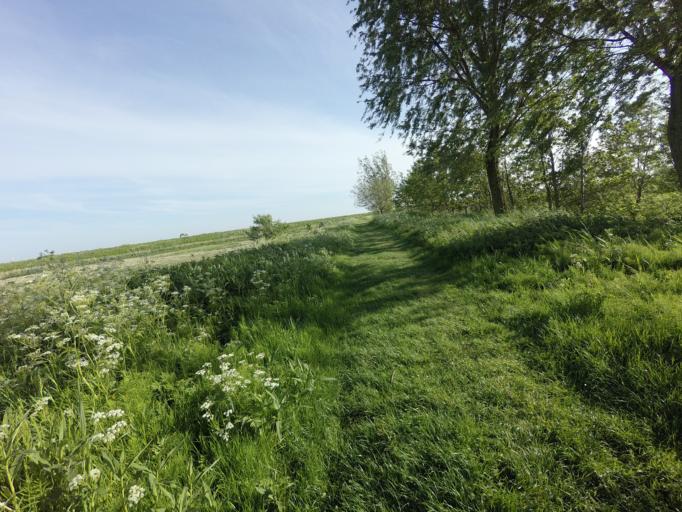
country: NL
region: North Brabant
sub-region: Gemeente Moerdijk
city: Willemstad
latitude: 51.7322
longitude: 4.3512
